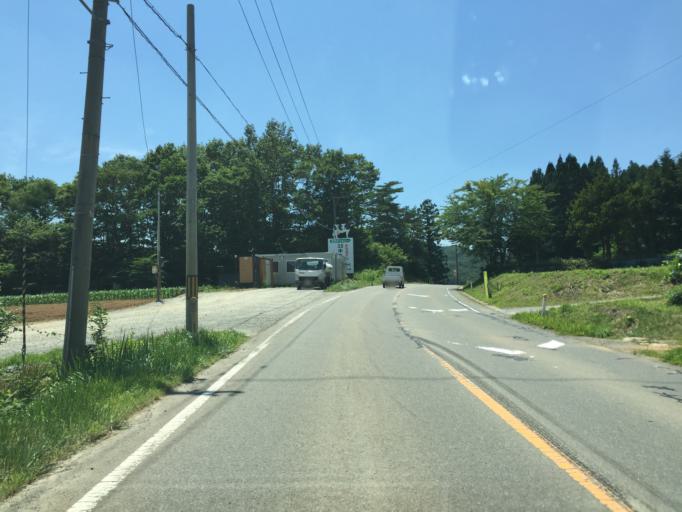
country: JP
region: Miyagi
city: Marumori
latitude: 37.7694
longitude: 140.7443
